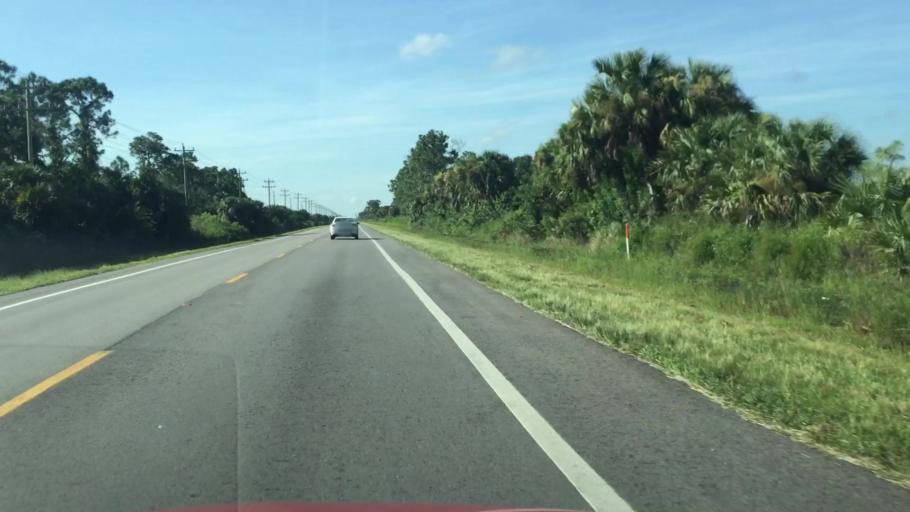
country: US
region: Florida
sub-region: Collier County
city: Immokalee
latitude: 26.3952
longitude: -81.4172
